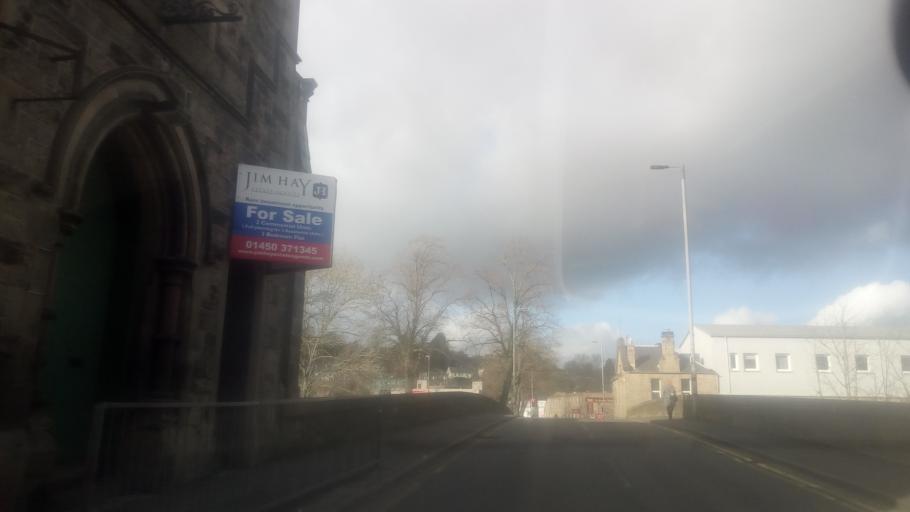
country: GB
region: Scotland
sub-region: The Scottish Borders
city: Hawick
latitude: 55.4219
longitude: -2.7900
